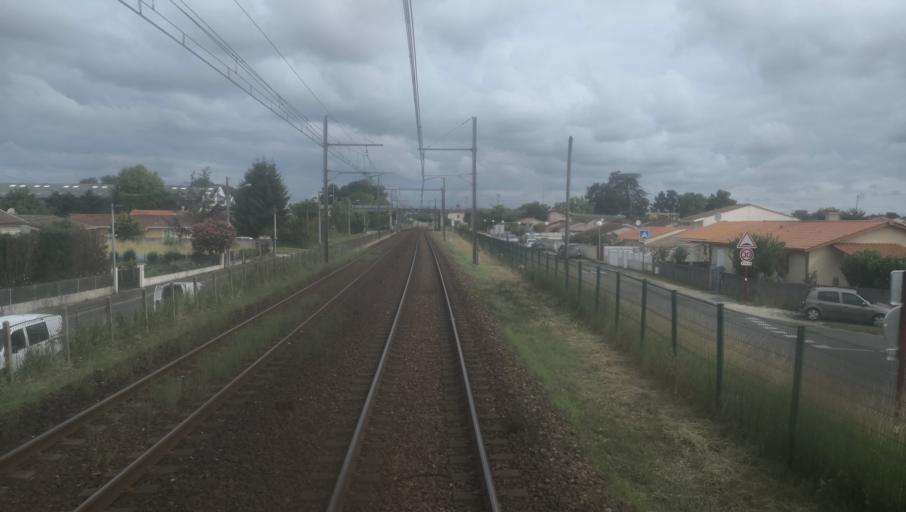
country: FR
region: Aquitaine
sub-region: Departement de la Gironde
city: Villenave-d'Ornon
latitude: 44.7659
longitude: -0.5459
